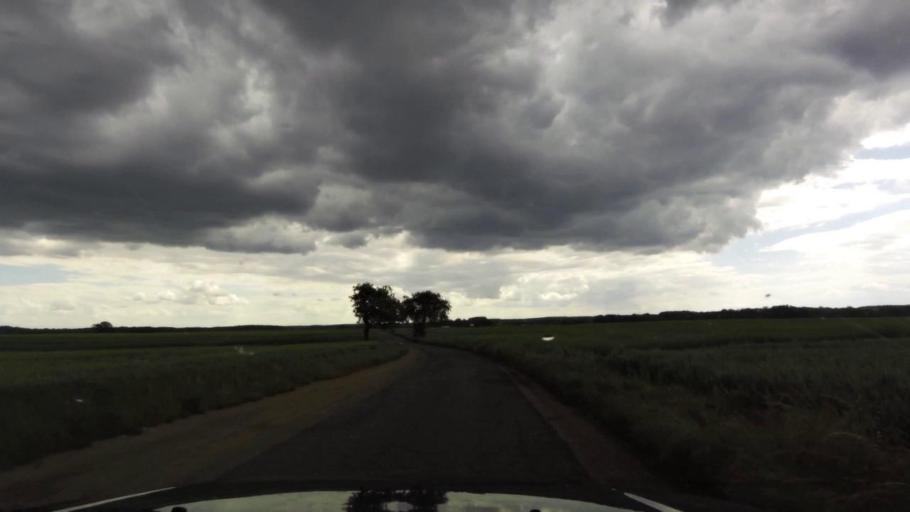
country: PL
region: West Pomeranian Voivodeship
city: Trzcinsko Zdroj
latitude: 52.9514
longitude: 14.6062
